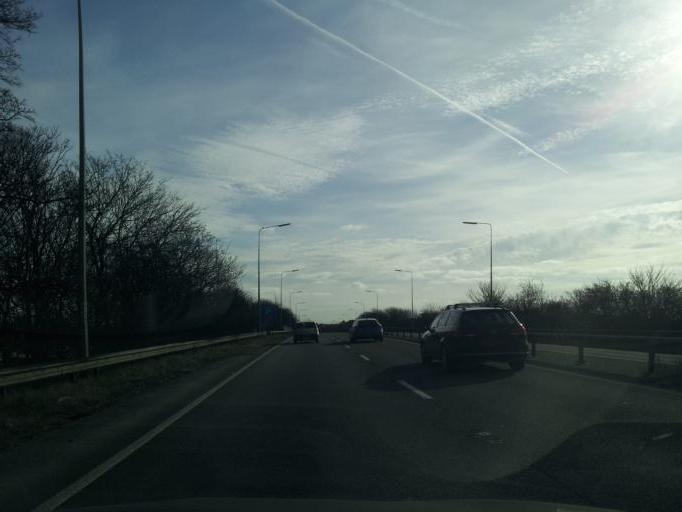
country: GB
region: England
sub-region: Central Bedfordshire
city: Biggleswade
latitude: 52.0775
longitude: -0.2630
